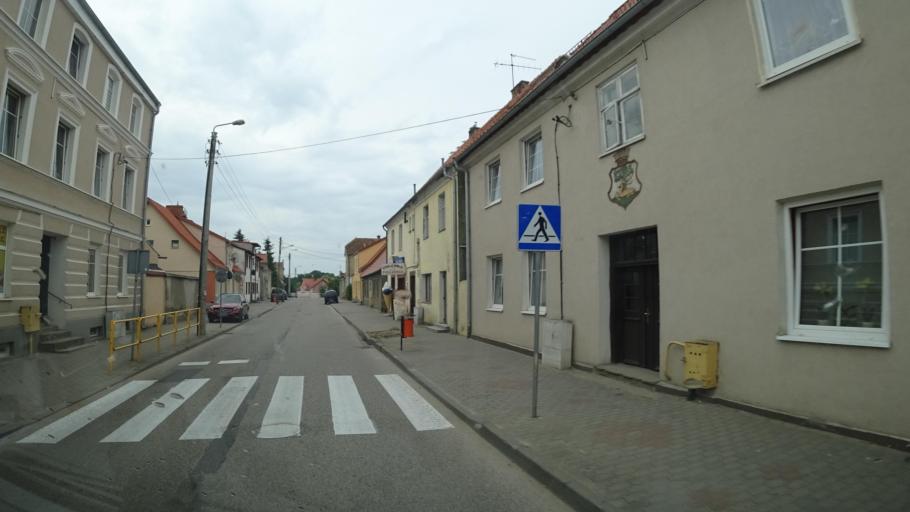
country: PL
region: Warmian-Masurian Voivodeship
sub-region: Powiat gizycki
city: Ryn
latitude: 53.9369
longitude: 21.5473
